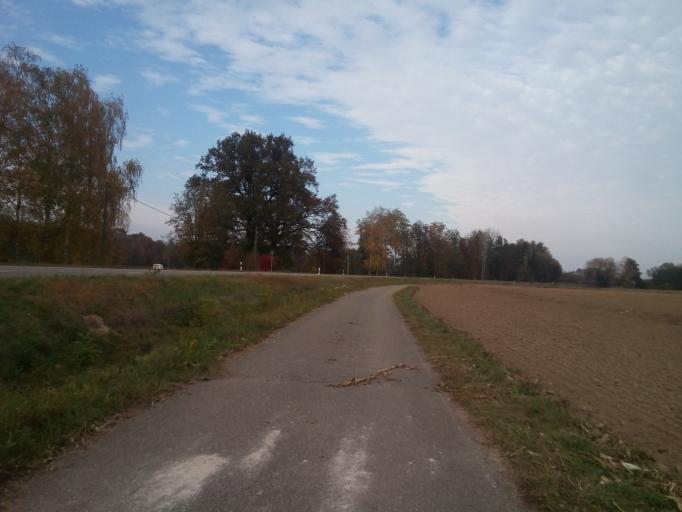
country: DE
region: Baden-Wuerttemberg
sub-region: Karlsruhe Region
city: Zell
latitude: 48.6748
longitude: 8.0210
